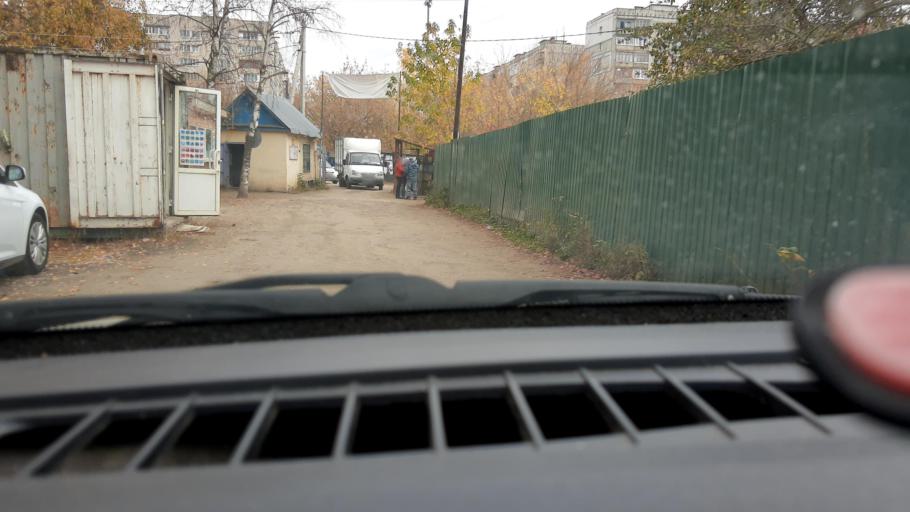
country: RU
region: Nizjnij Novgorod
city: Gorbatovka
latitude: 56.2589
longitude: 43.8436
